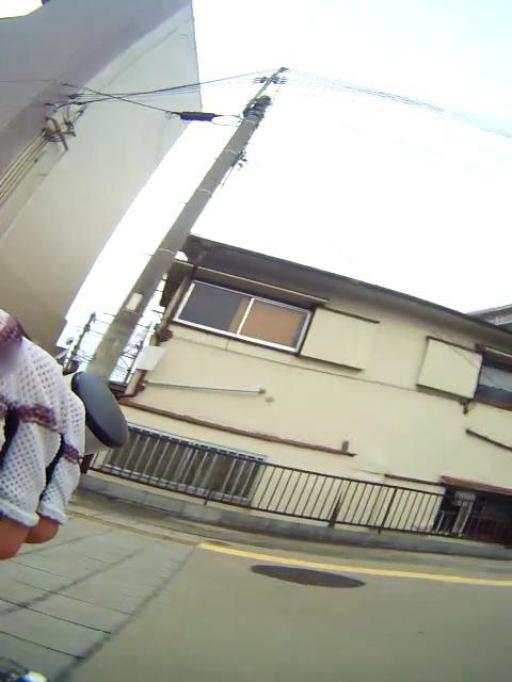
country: JP
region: Osaka
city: Kadoma
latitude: 34.7328
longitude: 135.5799
